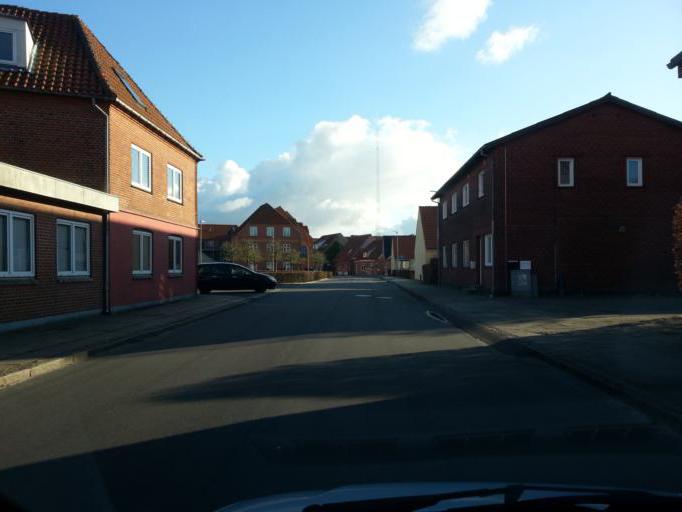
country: DK
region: South Denmark
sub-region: Varde Kommune
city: Olgod
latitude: 55.8097
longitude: 8.6200
